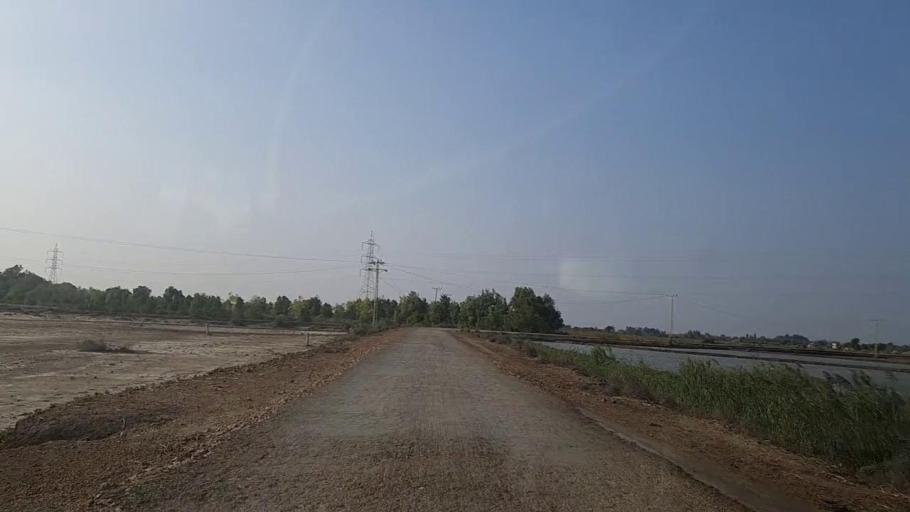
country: PK
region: Sindh
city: Mirpur Sakro
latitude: 24.5627
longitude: 67.6707
